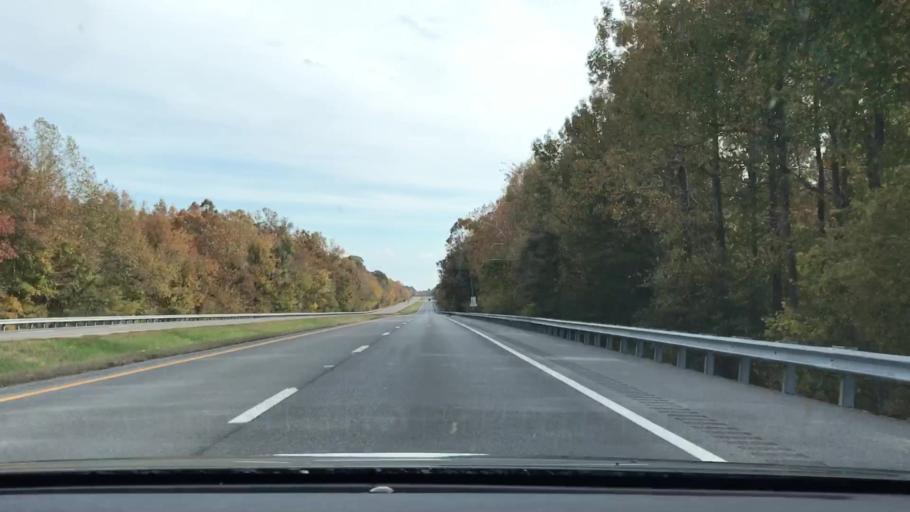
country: US
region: Kentucky
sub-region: Marshall County
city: Benton
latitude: 36.8321
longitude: -88.4430
